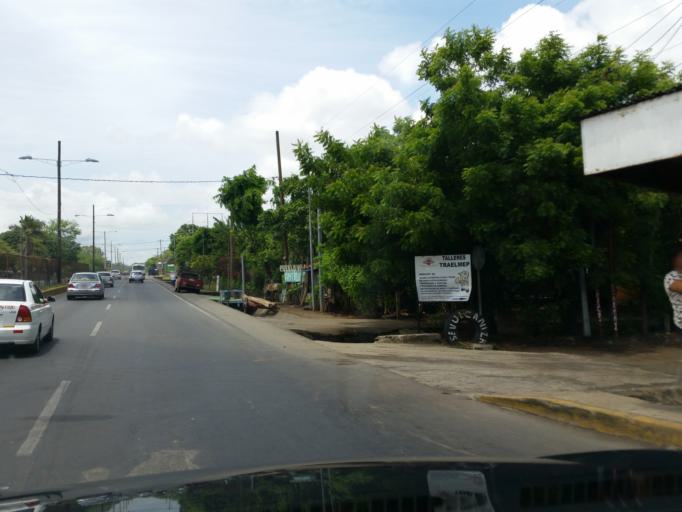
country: NI
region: Masaya
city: Ticuantepe
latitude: 12.0384
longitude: -86.1873
